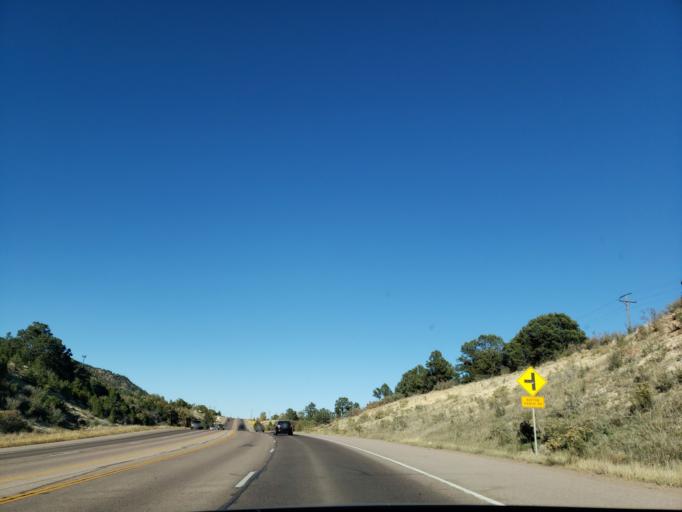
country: US
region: Colorado
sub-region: El Paso County
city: Fort Carson
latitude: 38.6746
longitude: -104.8507
